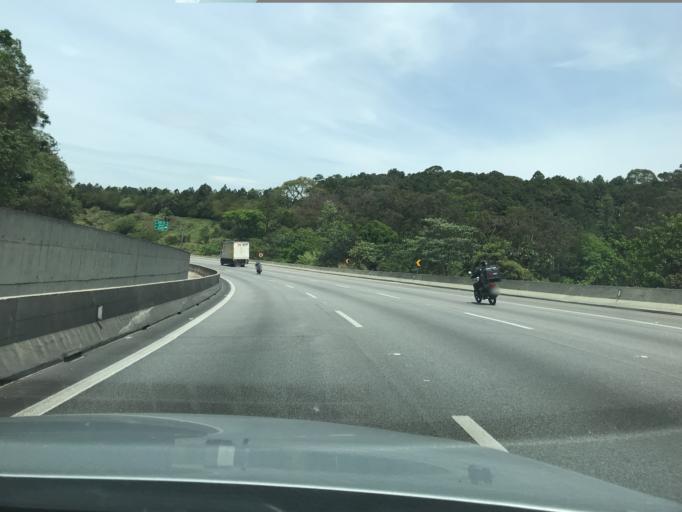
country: BR
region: Sao Paulo
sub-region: Osasco
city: Osasco
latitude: -23.4701
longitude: -46.7792
